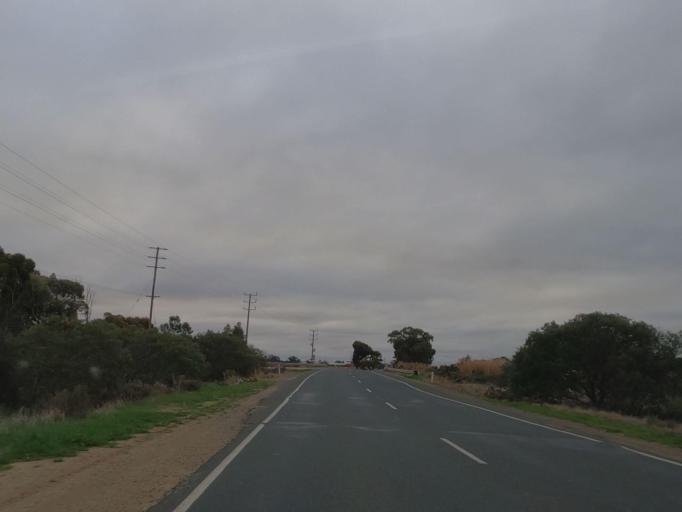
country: AU
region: Victoria
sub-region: Swan Hill
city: Swan Hill
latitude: -35.3959
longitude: 143.5732
